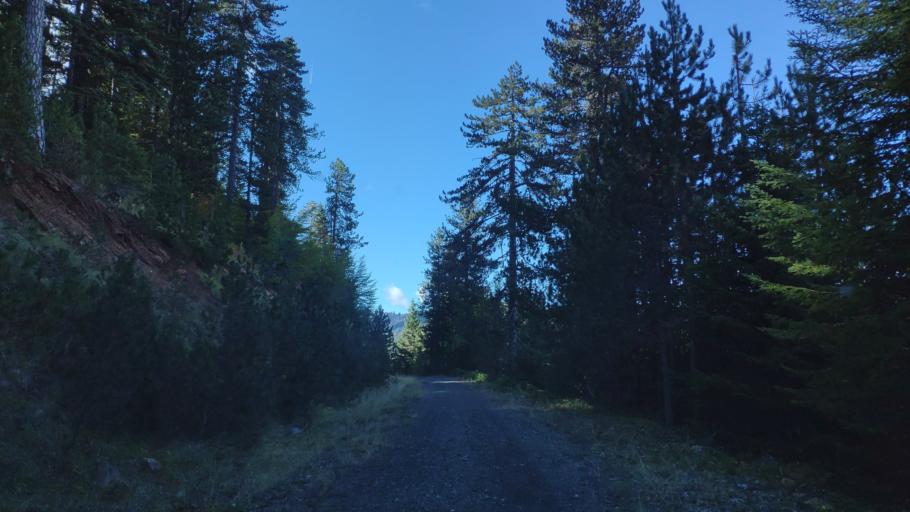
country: GR
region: Epirus
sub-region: Nomos Ioanninon
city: Metsovo
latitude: 39.8912
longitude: 21.2093
